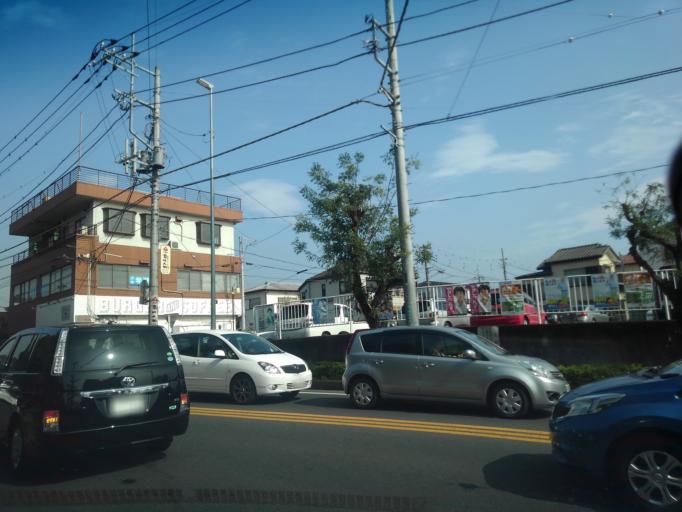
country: JP
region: Saitama
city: Tokorozawa
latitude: 35.7980
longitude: 139.4800
